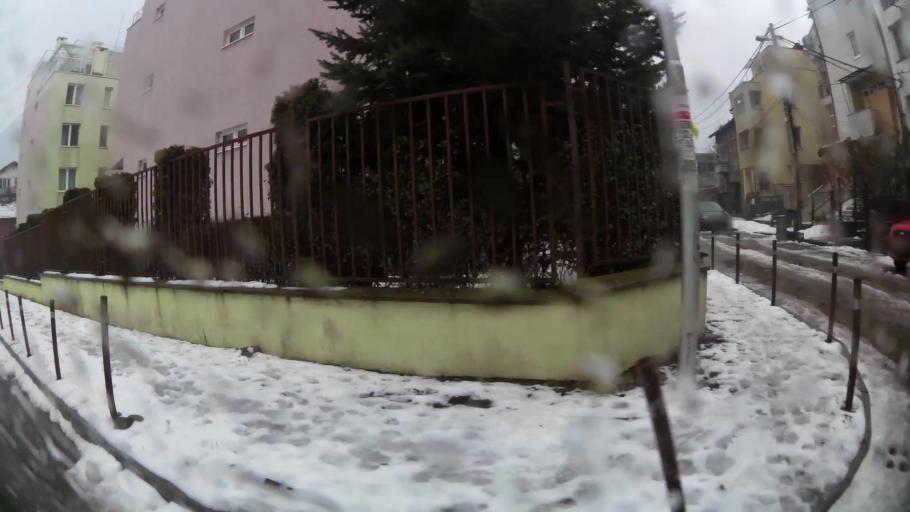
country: BG
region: Sofia-Capital
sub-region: Stolichna Obshtina
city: Sofia
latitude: 42.6813
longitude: 23.2642
